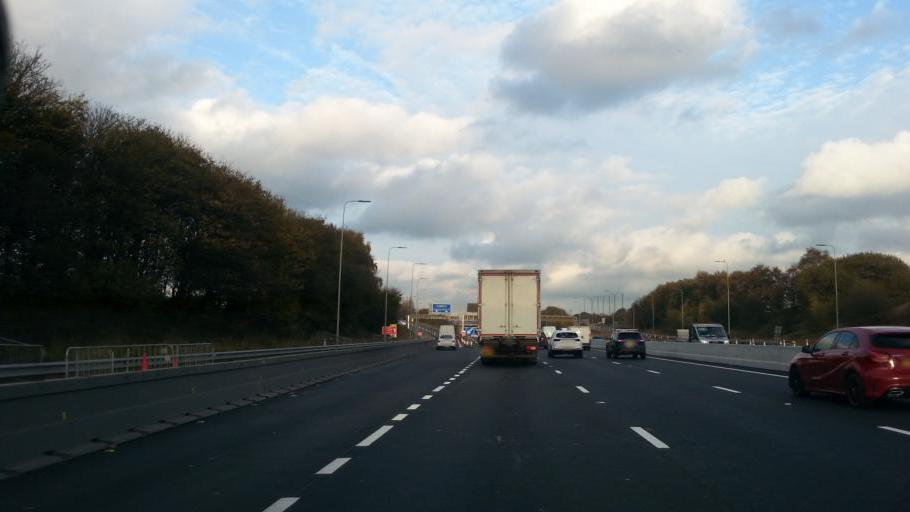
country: GB
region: England
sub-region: Manchester
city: Heywood
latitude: 53.5733
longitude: -2.2142
